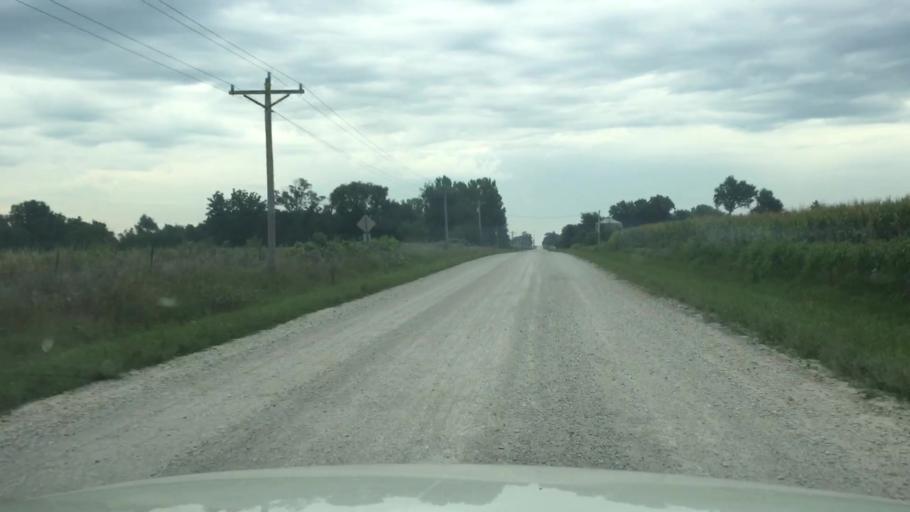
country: US
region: Iowa
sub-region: Story County
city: Huxley
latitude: 41.8905
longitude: -93.5809
